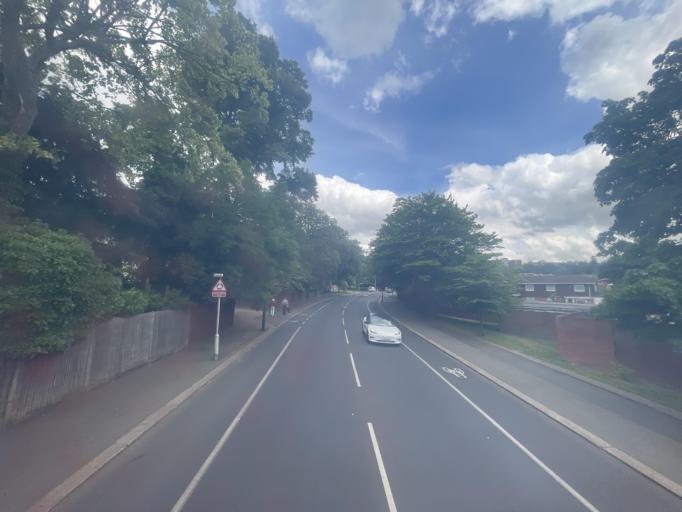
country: GB
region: England
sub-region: Greater London
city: Thornton Heath
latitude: 51.4279
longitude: -0.0842
